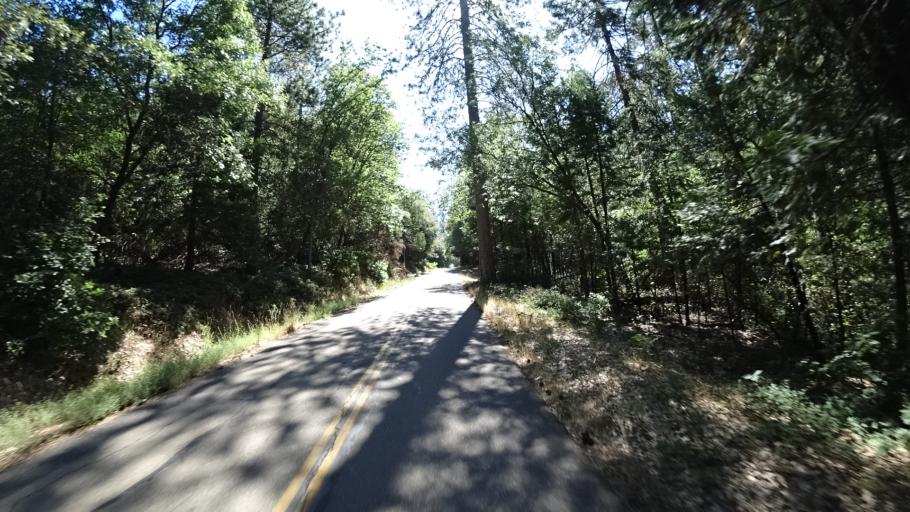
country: US
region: California
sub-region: Amador County
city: Pioneer
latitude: 38.3976
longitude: -120.4948
